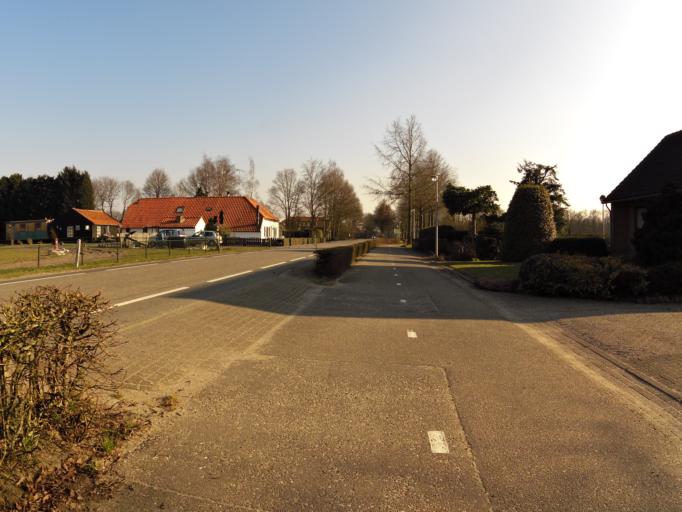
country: NL
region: North Brabant
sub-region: Gemeente Maasdonk
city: Geffen
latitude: 51.7102
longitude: 5.4356
